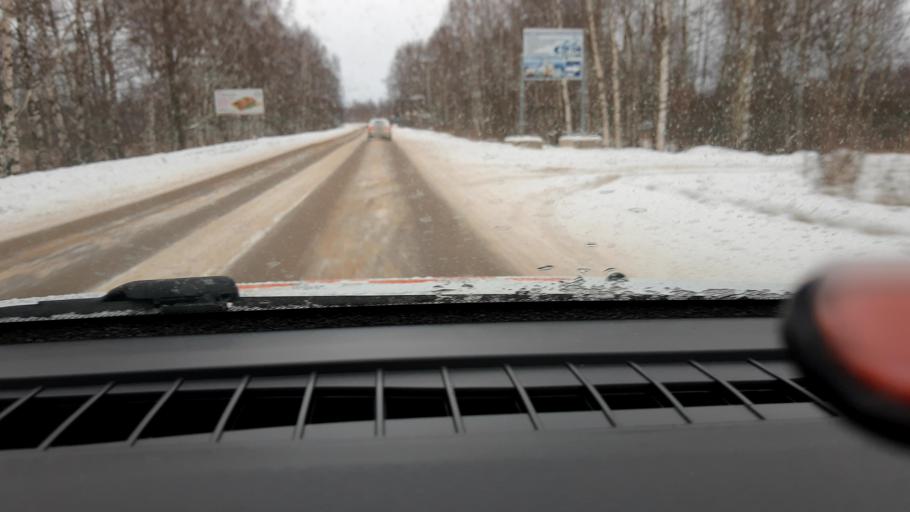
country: RU
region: Nizjnij Novgorod
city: Afonino
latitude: 56.3148
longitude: 44.2183
